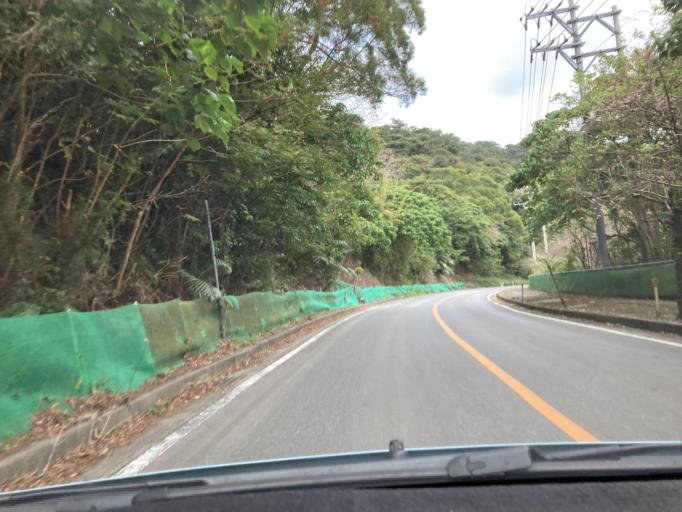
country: JP
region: Okinawa
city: Nago
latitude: 26.8317
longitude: 128.2793
